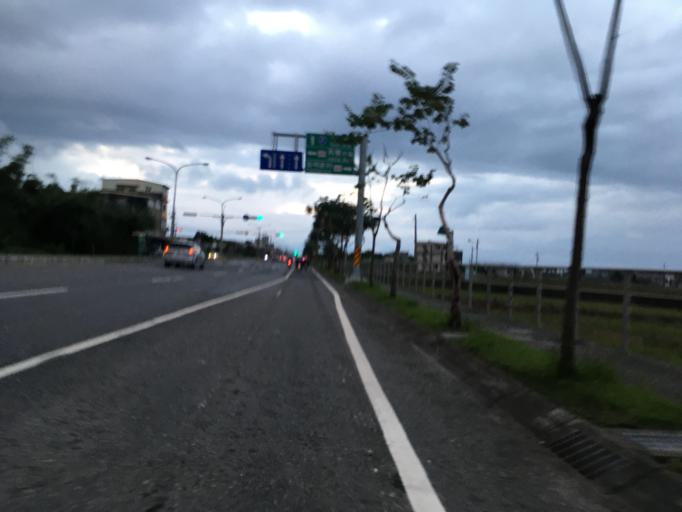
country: TW
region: Taiwan
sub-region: Yilan
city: Yilan
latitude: 24.6186
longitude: 121.8446
